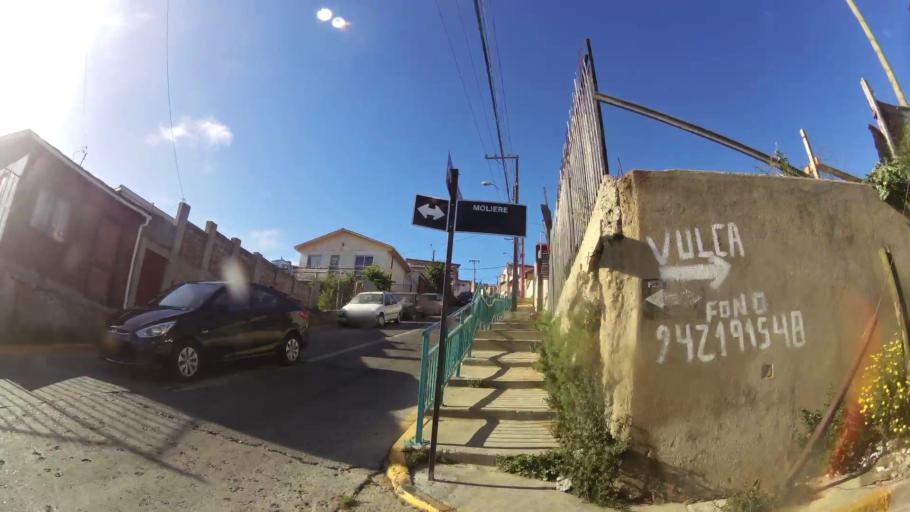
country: CL
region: Valparaiso
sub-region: Provincia de Valparaiso
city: Valparaiso
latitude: -33.0577
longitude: -71.6130
